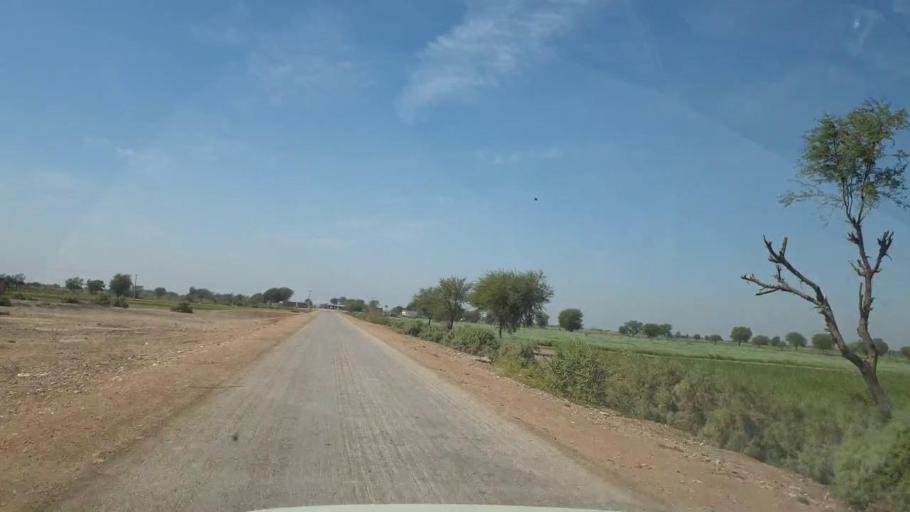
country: PK
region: Sindh
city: Mirpur Khas
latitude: 25.6472
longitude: 69.1729
